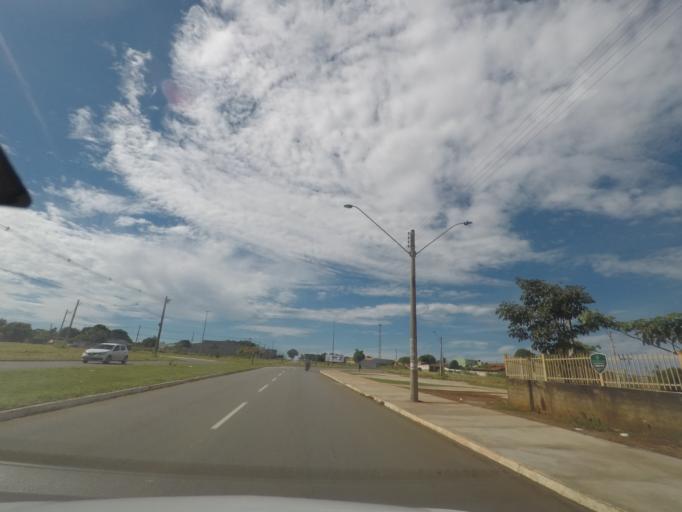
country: BR
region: Goias
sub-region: Aparecida De Goiania
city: Aparecida de Goiania
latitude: -16.8030
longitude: -49.2826
